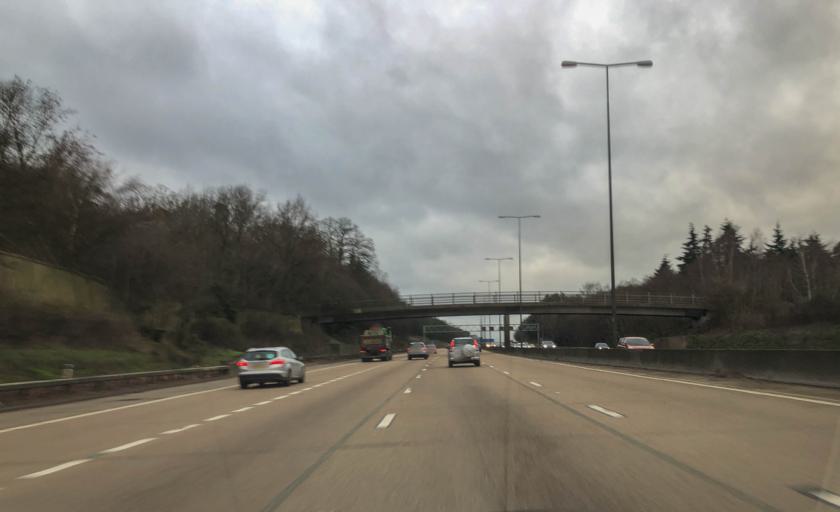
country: GB
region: England
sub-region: Surrey
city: Cobham
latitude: 51.3144
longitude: -0.4326
